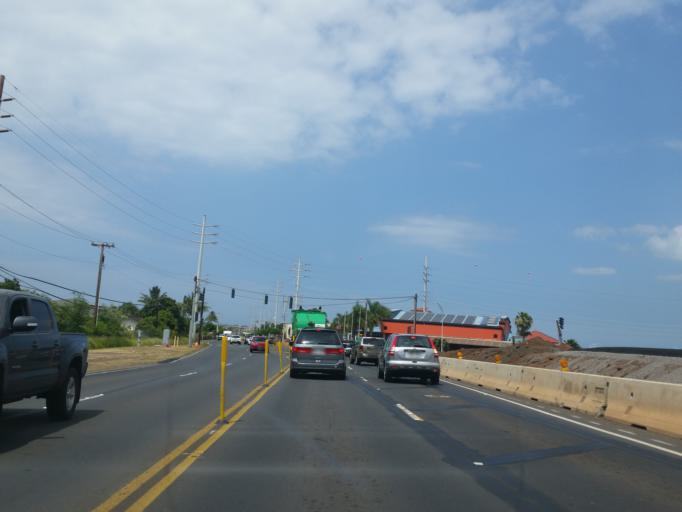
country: US
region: Hawaii
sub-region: Maui County
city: Kahului
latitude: 20.8782
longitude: -156.4586
